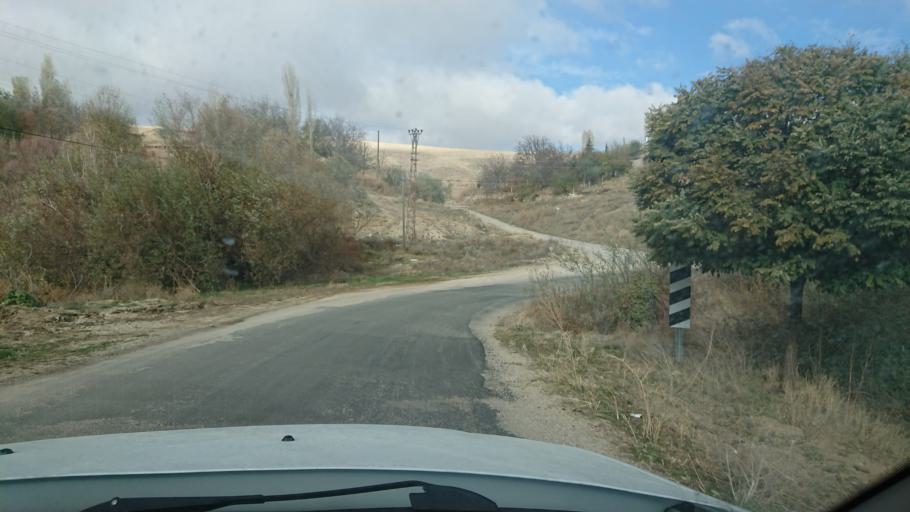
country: TR
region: Aksaray
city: Ortakoy
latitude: 38.8050
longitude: 33.9822
